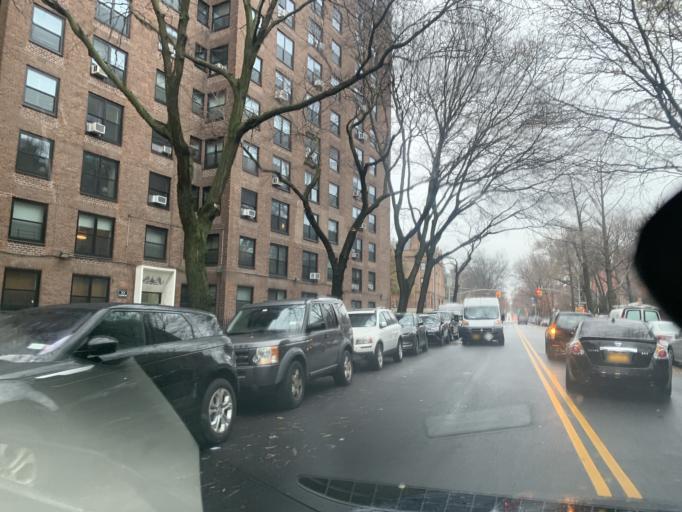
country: US
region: New York
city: New York City
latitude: 40.6924
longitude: -73.9686
